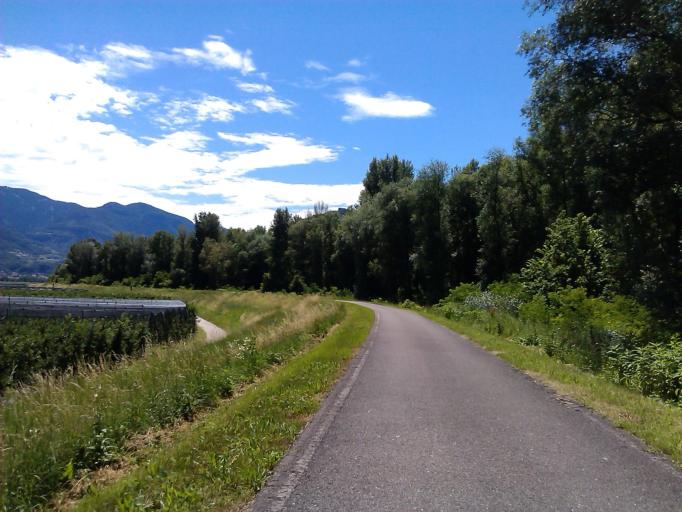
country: IT
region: Trentino-Alto Adige
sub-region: Bolzano
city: Vadena
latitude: 46.3944
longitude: 11.2980
